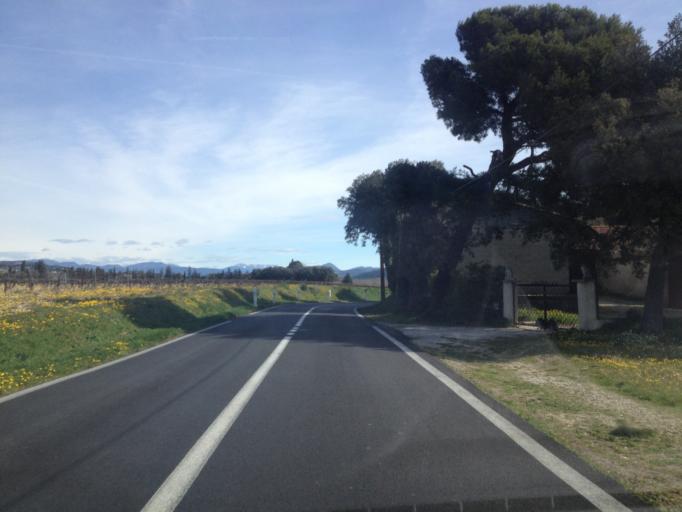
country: FR
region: Provence-Alpes-Cote d'Azur
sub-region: Departement du Vaucluse
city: Sablet
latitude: 44.1963
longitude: 4.9748
